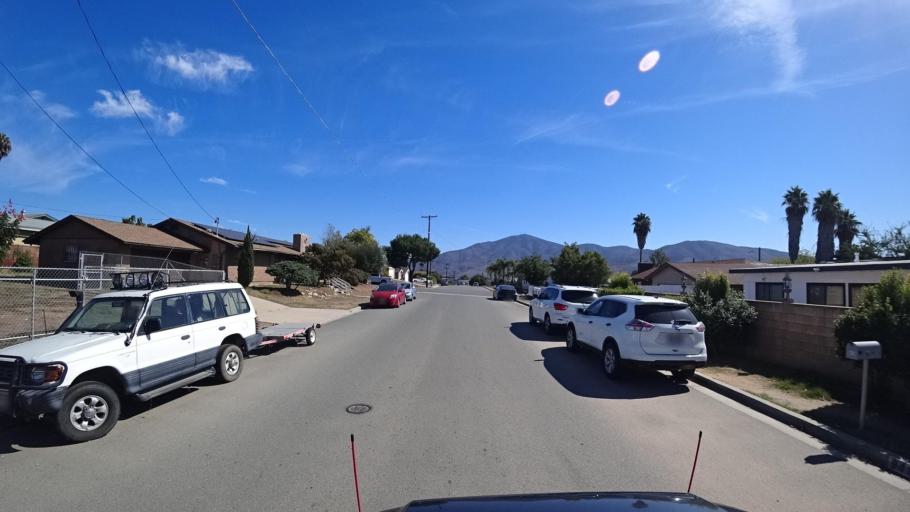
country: US
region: California
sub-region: San Diego County
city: La Presa
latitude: 32.7060
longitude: -116.9969
